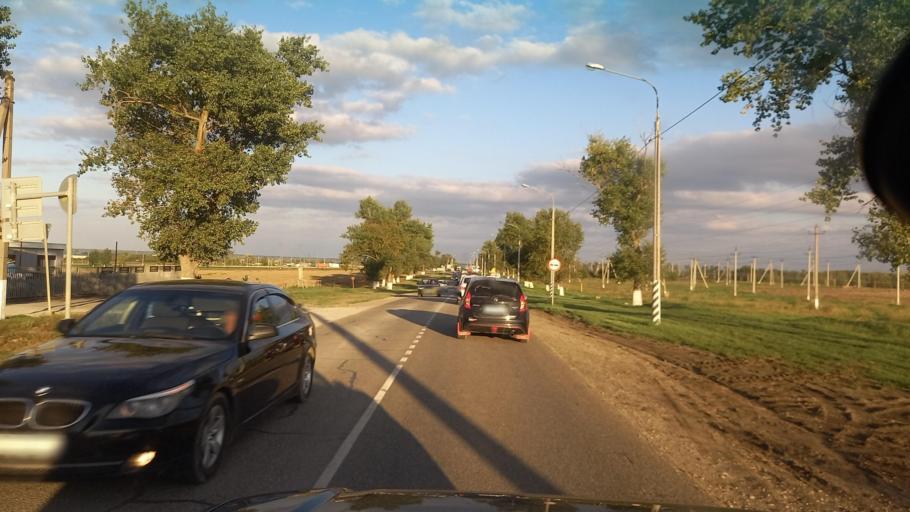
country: RU
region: Krasnodarskiy
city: Krymsk
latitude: 44.9381
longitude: 37.9554
